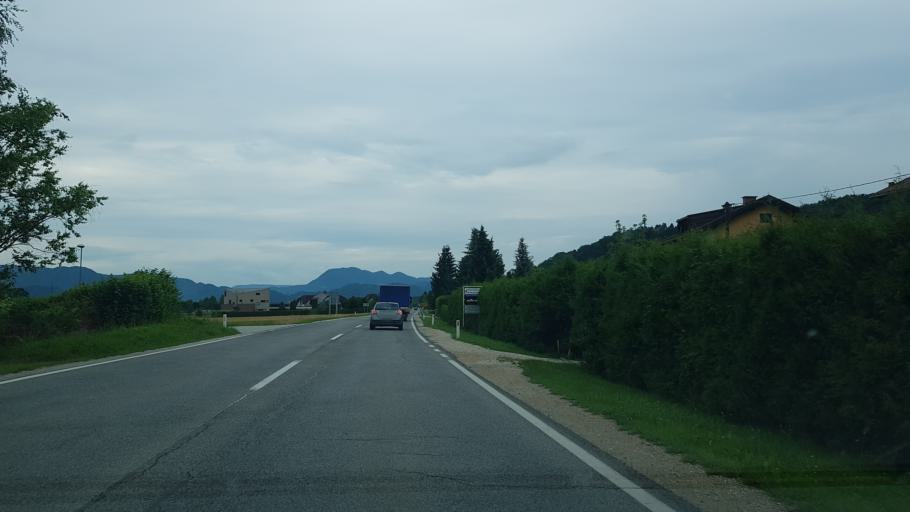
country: SI
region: Vojnik
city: Vojnik
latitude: 46.2766
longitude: 15.2987
